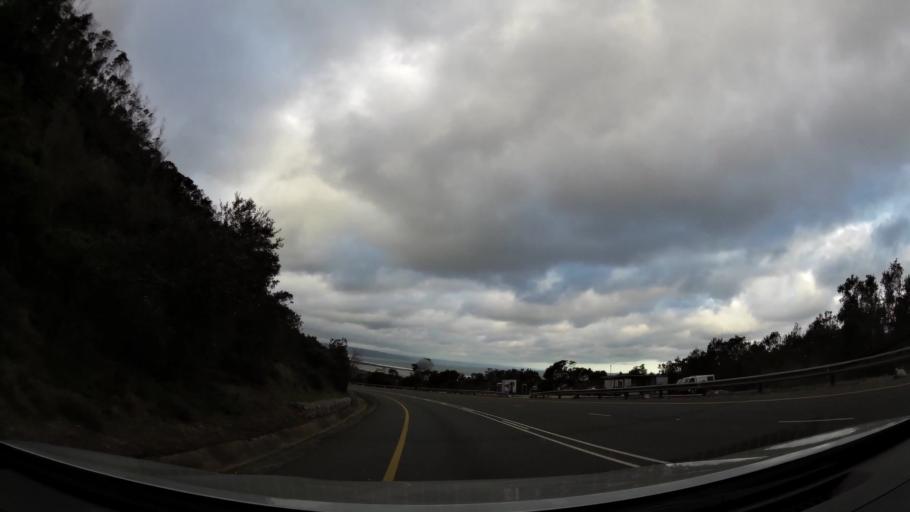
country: ZA
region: Western Cape
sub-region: Eden District Municipality
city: Plettenberg Bay
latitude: -34.0440
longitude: 23.3661
